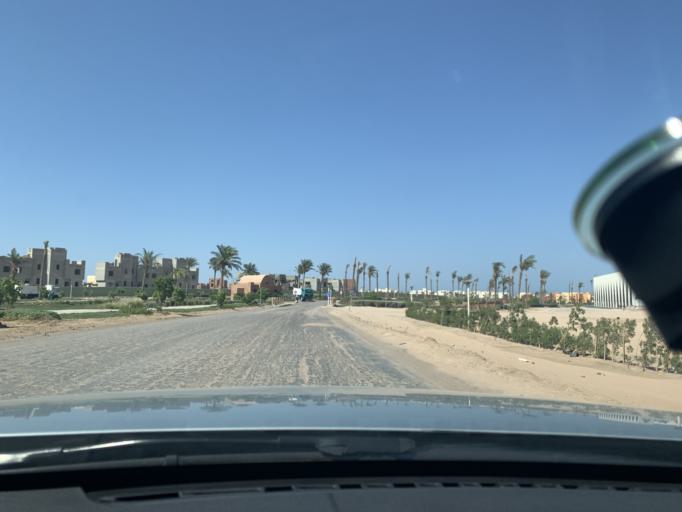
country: EG
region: Red Sea
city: El Gouna
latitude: 27.4031
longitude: 33.6648
